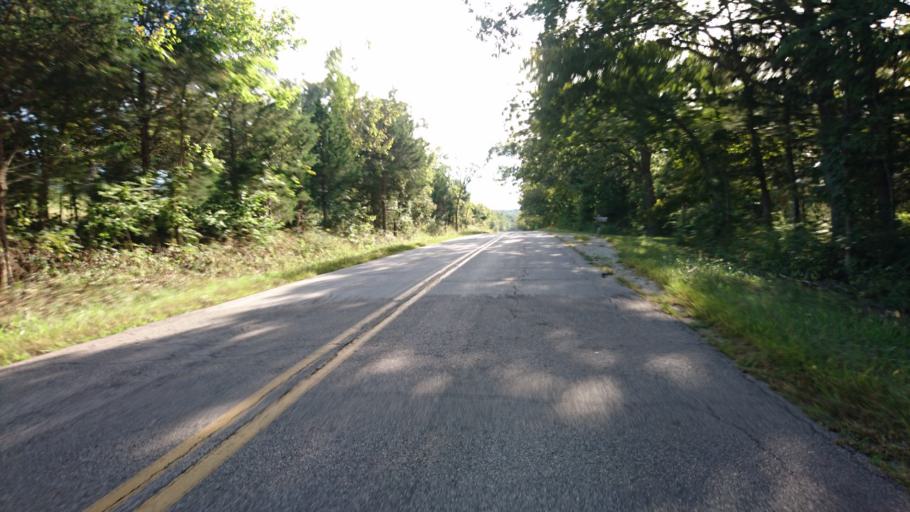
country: US
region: Missouri
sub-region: Crawford County
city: Cuba
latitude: 38.1030
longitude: -91.3476
